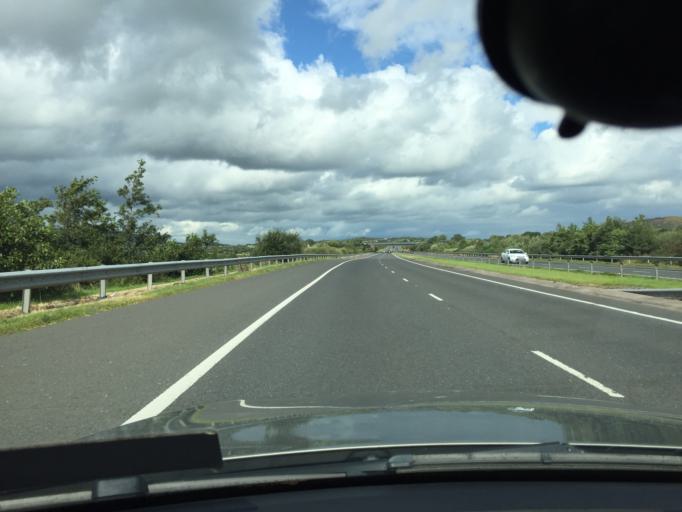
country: GB
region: Northern Ireland
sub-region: Newry and Mourne District
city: Newry
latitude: 54.1150
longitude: -6.3648
